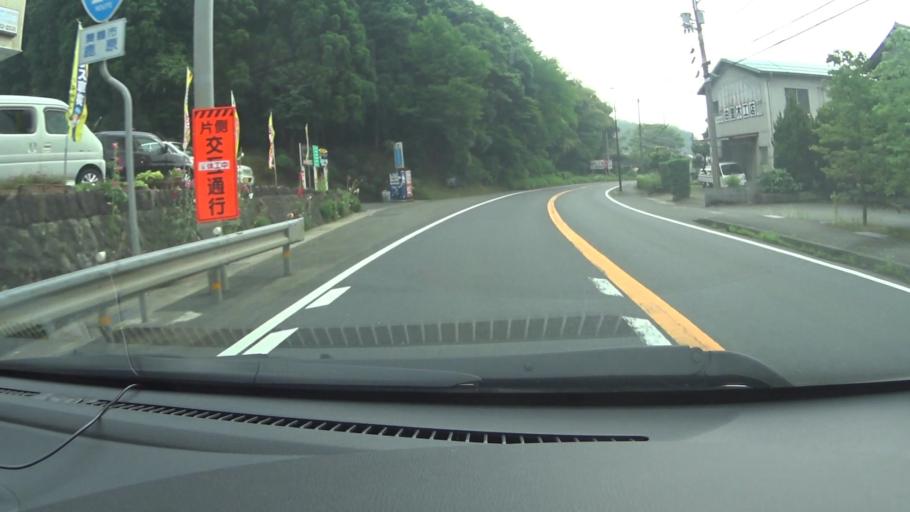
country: JP
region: Kyoto
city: Maizuru
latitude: 35.4819
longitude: 135.4436
